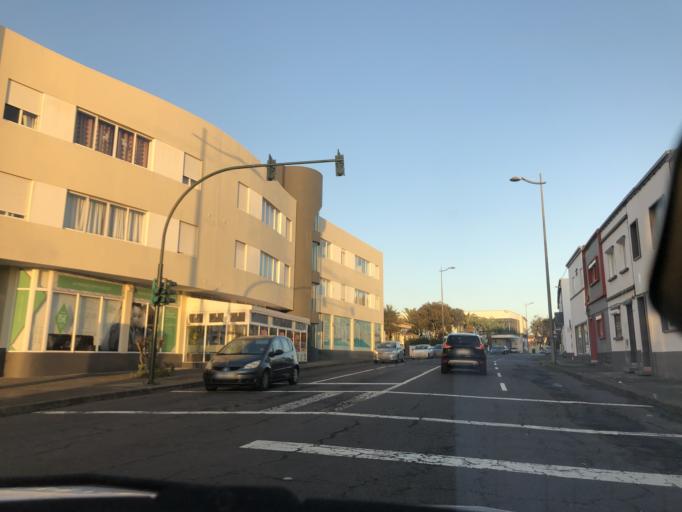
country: PT
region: Azores
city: Ponta Delgada
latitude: 37.7480
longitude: -25.6654
